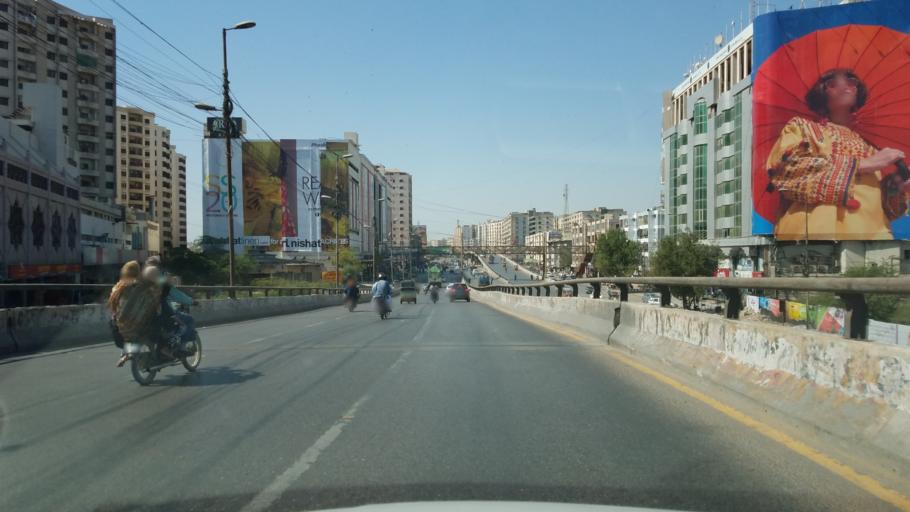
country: PK
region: Sindh
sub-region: Karachi District
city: Karachi
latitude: 24.9014
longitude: 67.1160
